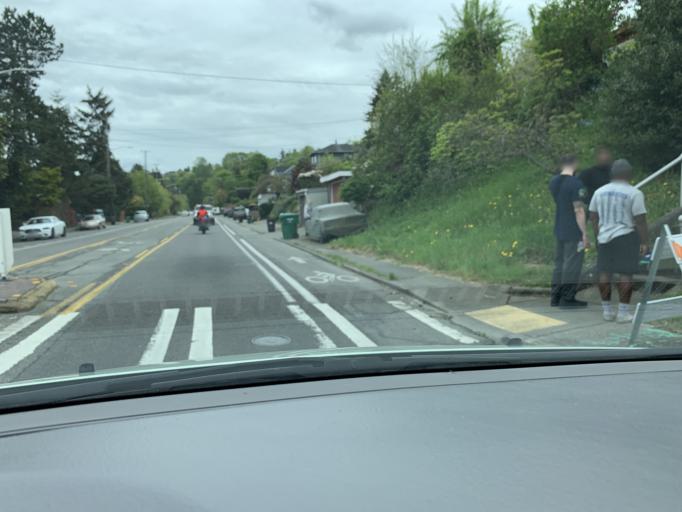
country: US
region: Washington
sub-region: King County
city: Bryn Mawr-Skyway
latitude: 47.5133
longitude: -122.2507
